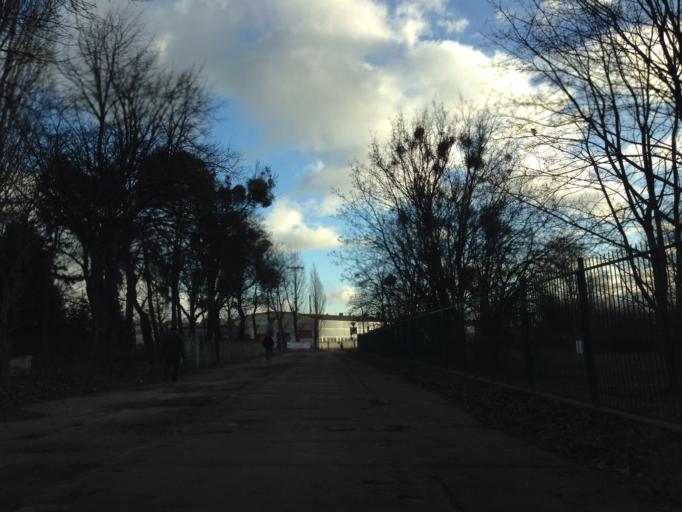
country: PL
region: Pomeranian Voivodeship
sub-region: Gdansk
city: Gdansk
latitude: 54.3978
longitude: 18.6171
